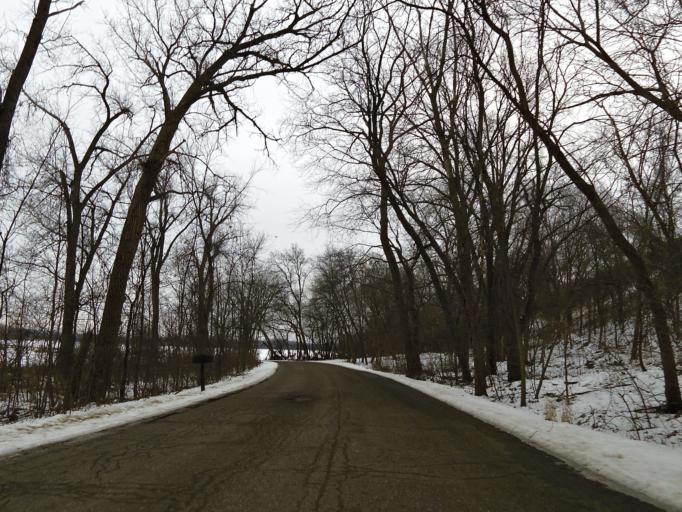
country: US
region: Minnesota
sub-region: Dakota County
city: Mendota Heights
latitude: 44.8871
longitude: -93.1856
